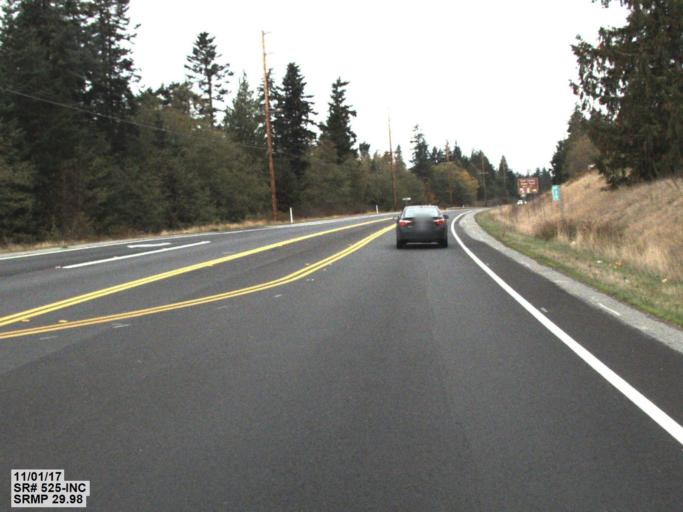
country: US
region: Washington
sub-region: Island County
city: Camano
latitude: 48.1637
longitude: -122.6065
